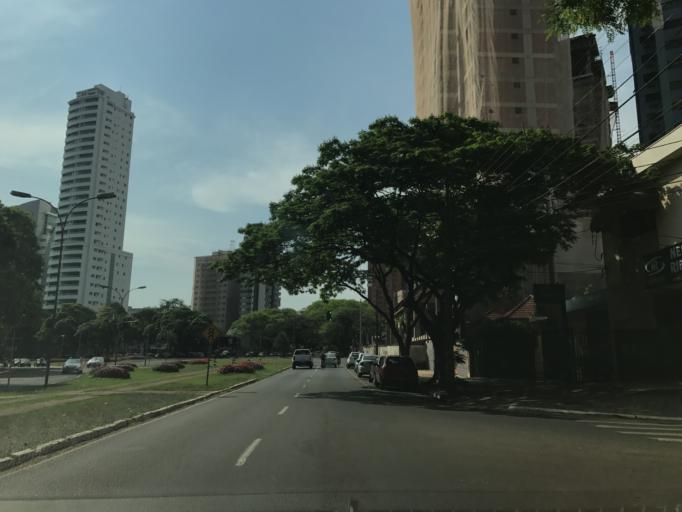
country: BR
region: Parana
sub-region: Maringa
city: Maringa
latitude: -23.4247
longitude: -51.9277
